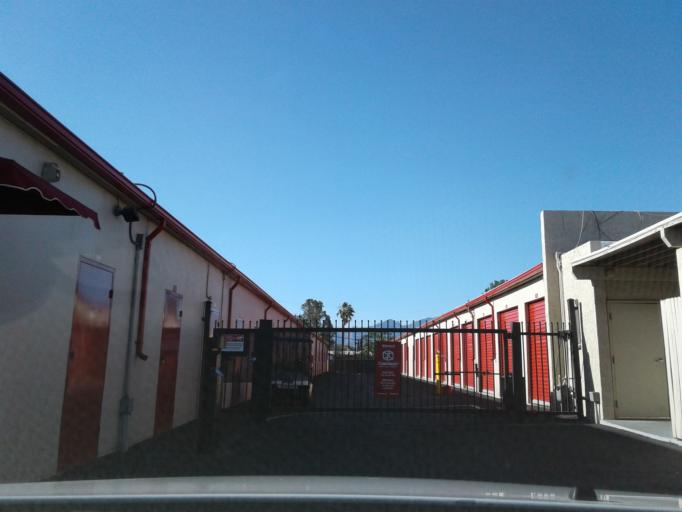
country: US
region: Arizona
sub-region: Pima County
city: Tucson
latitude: 32.1999
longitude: -110.9072
